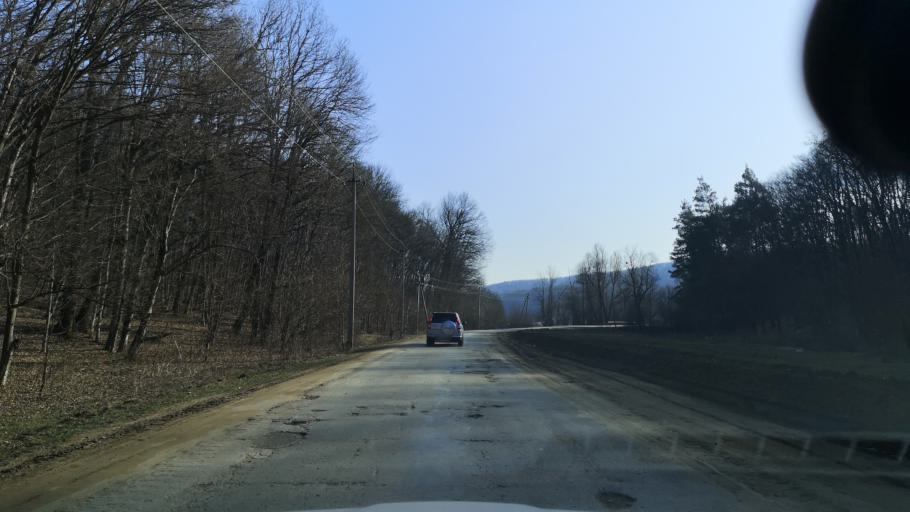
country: MD
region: Nisporeni
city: Nisporeni
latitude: 47.0854
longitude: 28.3212
